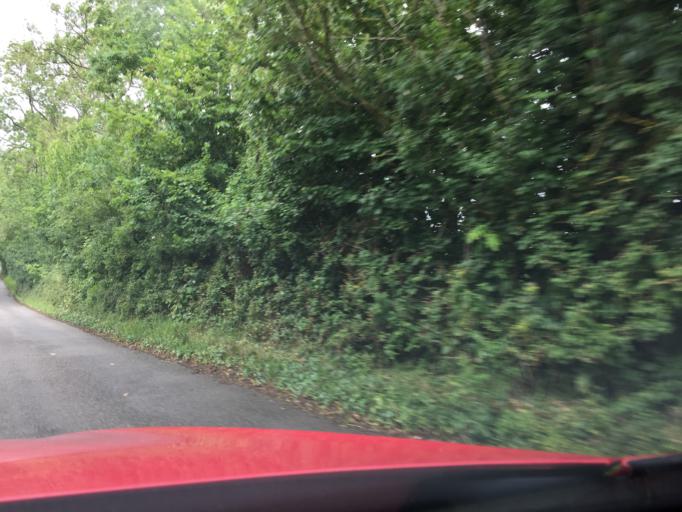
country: GB
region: England
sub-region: Northamptonshire
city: Daventry
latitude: 52.2348
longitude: -1.1565
